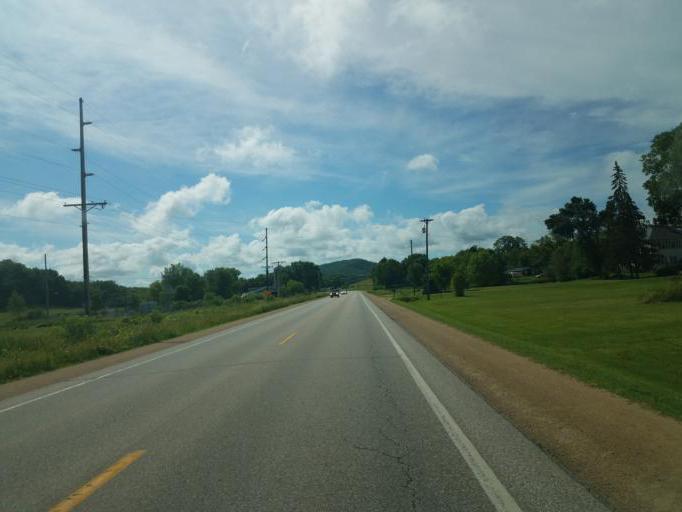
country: US
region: Wisconsin
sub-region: Monroe County
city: Tomah
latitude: 43.8304
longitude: -90.4656
